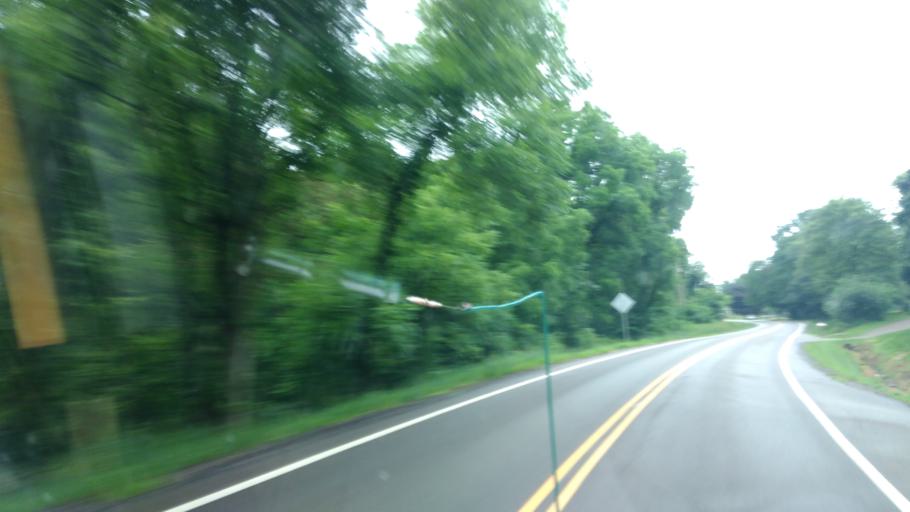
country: US
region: Ohio
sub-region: Stark County
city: Minerva
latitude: 40.6744
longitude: -81.0307
